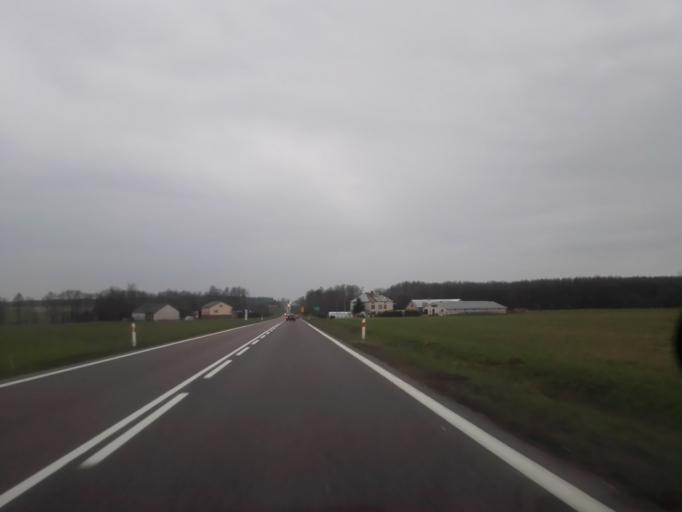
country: PL
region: Podlasie
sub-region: Powiat grajewski
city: Szczuczyn
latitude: 53.4931
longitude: 22.2257
